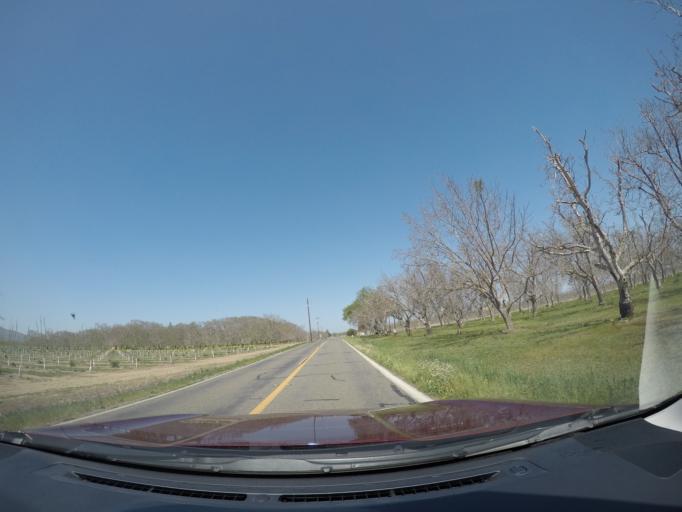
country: US
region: California
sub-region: Yolo County
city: Winters
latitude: 38.5022
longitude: -121.9575
